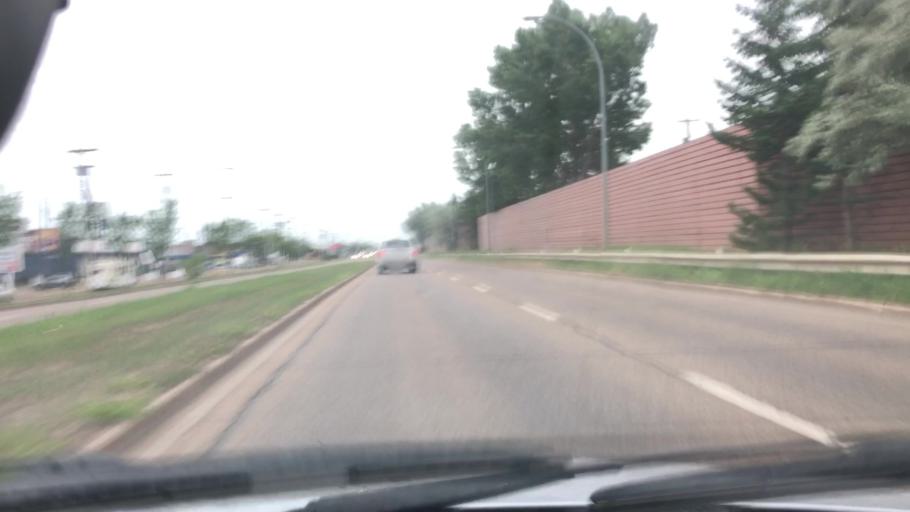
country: CA
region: Alberta
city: St. Albert
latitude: 53.5589
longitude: -113.5976
